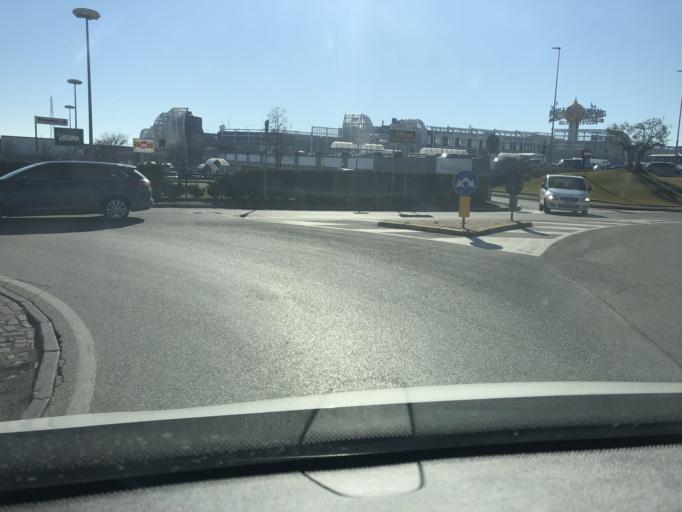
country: IT
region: Veneto
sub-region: Provincia di Verona
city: Lugagnano
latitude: 45.4413
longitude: 10.8660
